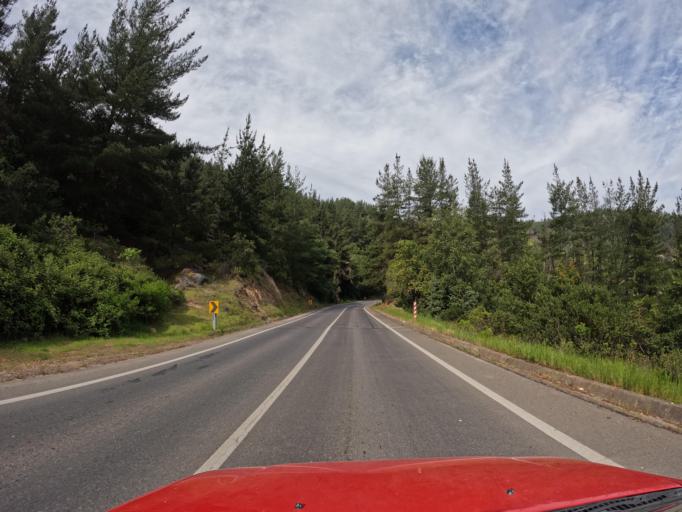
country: CL
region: Maule
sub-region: Provincia de Talca
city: Talca
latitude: -35.2973
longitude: -71.9649
